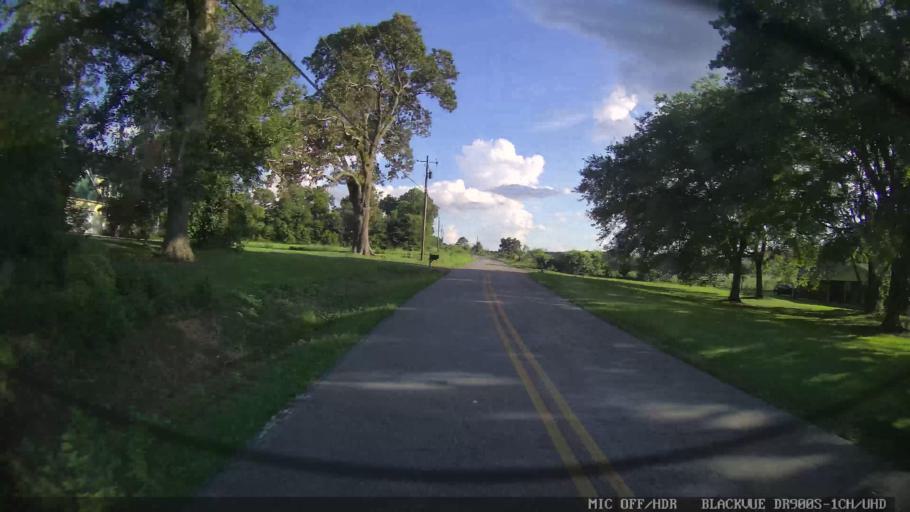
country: US
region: Georgia
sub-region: Bartow County
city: Rydal
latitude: 34.2766
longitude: -84.7544
